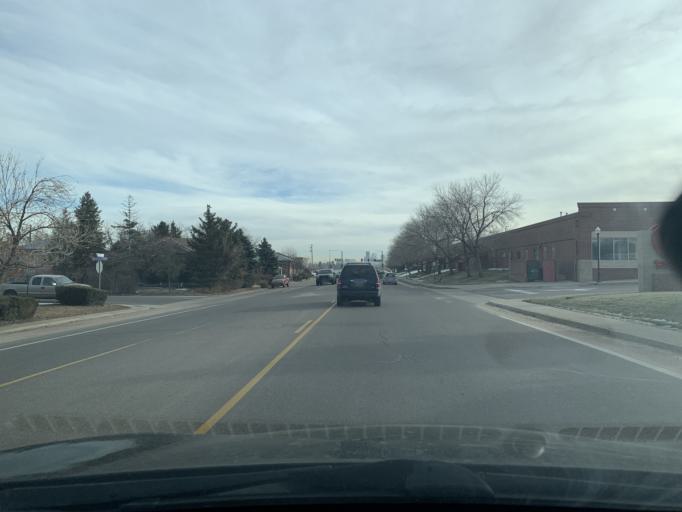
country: US
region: Colorado
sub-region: Jefferson County
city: Edgewater
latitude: 39.7476
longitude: -105.0561
